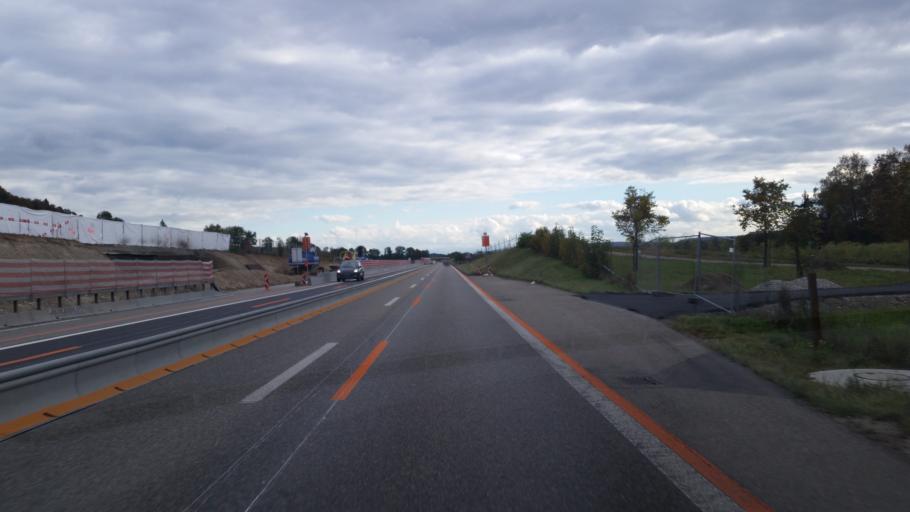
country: CH
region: Zurich
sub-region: Bezirk Buelach
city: Bachenbulach
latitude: 47.4878
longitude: 8.5438
